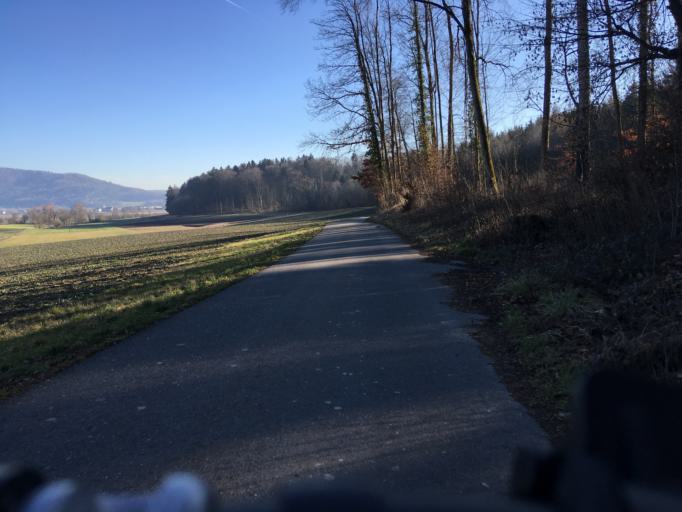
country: CH
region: Schaffhausen
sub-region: Bezirk Stein
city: Ramsen
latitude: 47.7255
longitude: 8.8023
